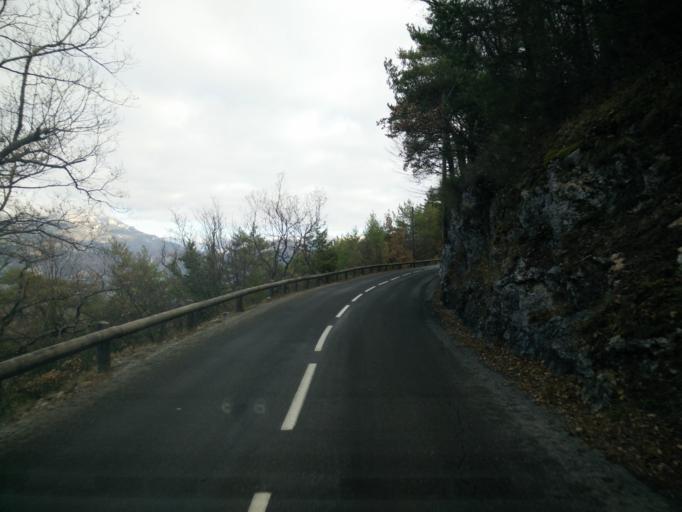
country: FR
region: Provence-Alpes-Cote d'Azur
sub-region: Departement des Alpes-Maritimes
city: Le Broc
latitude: 43.8193
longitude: 7.1333
